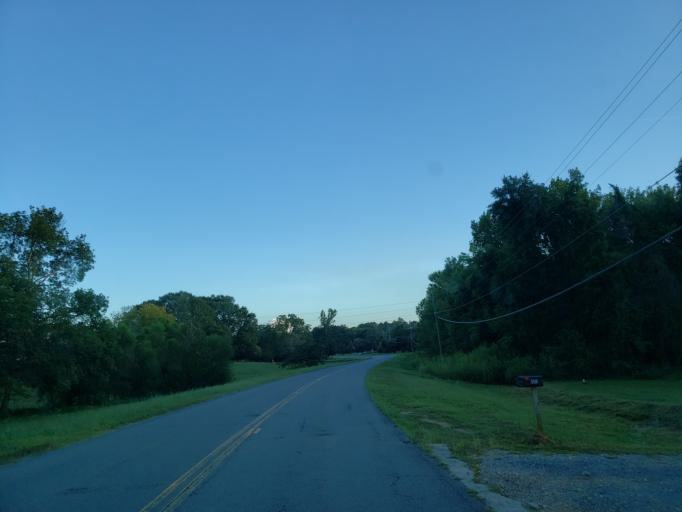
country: US
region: Georgia
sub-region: Floyd County
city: Rome
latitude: 34.2474
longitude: -85.1365
